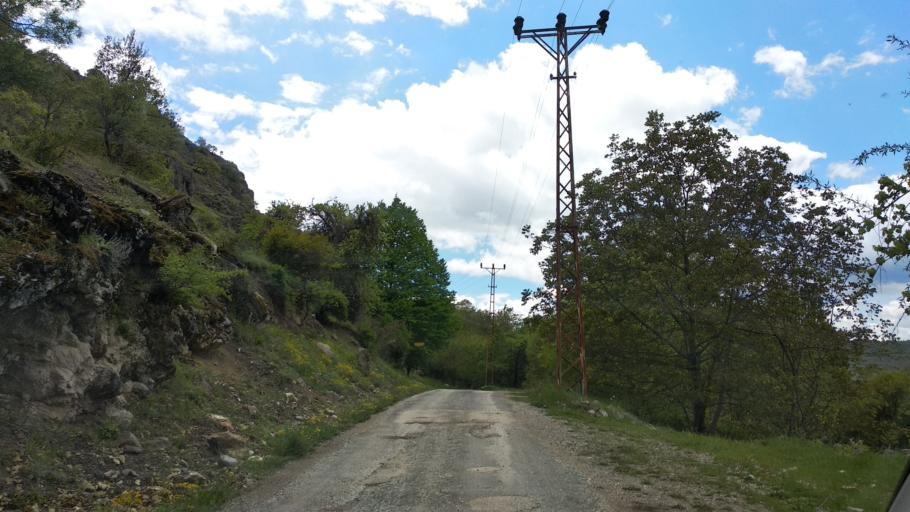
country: TR
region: Bolu
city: Seben
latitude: 40.4306
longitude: 31.6002
